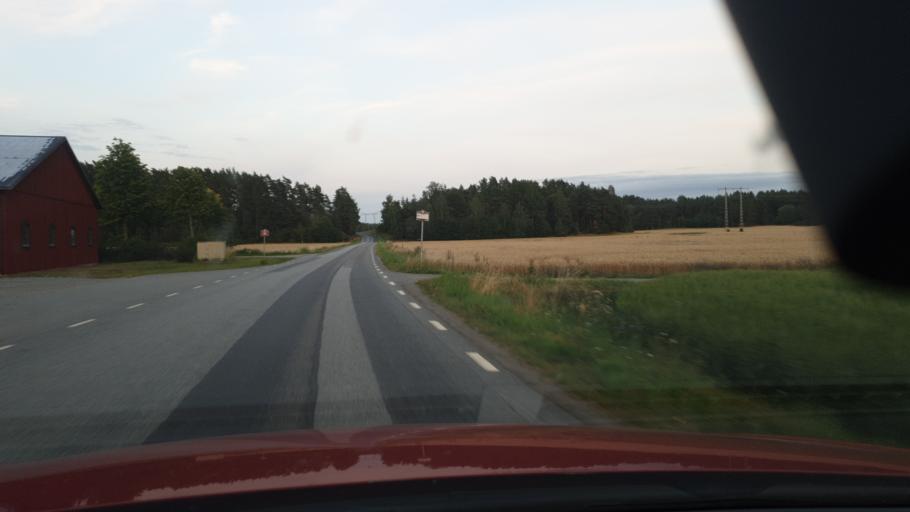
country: SE
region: Uppsala
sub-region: Enkopings Kommun
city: Orsundsbro
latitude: 59.6862
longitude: 17.3933
